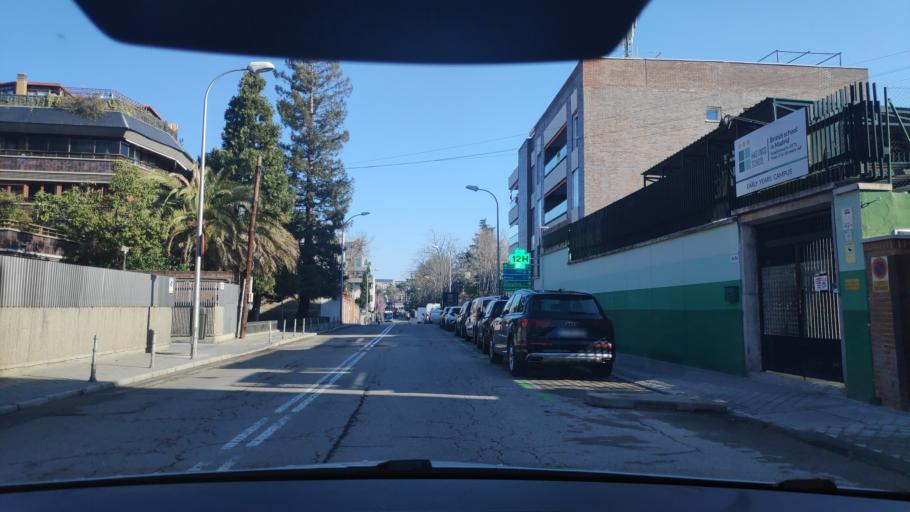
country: ES
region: Madrid
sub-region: Provincia de Madrid
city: Chamartin
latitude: 40.4647
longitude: -3.6796
